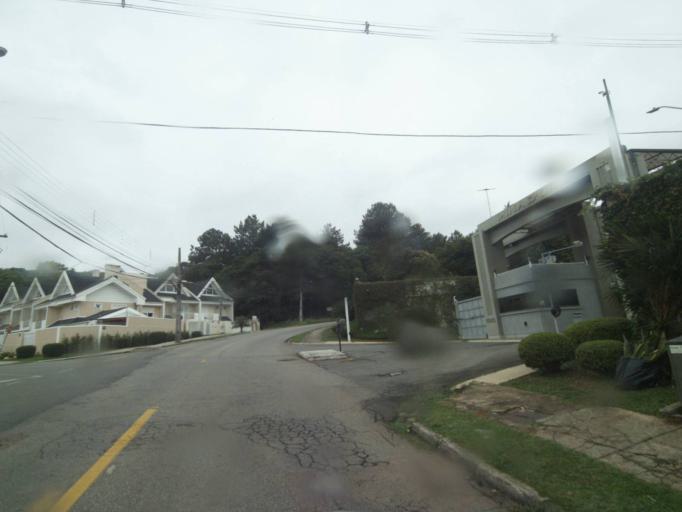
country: BR
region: Parana
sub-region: Curitiba
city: Curitiba
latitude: -25.4273
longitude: -49.3365
